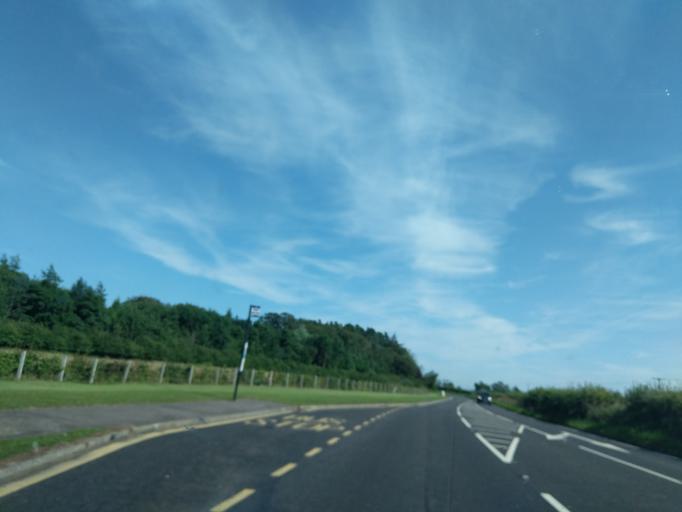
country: GB
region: Scotland
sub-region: Fife
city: Saint Andrews
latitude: 56.3178
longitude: -2.7386
